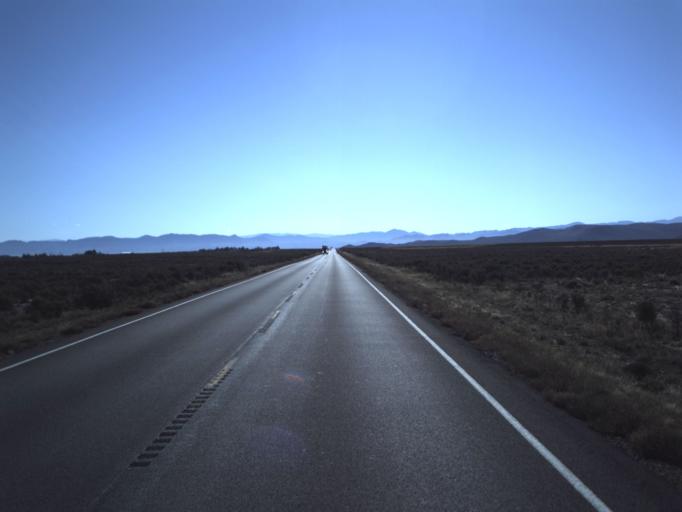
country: US
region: Utah
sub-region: Washington County
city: Enterprise
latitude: 37.7743
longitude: -113.8403
